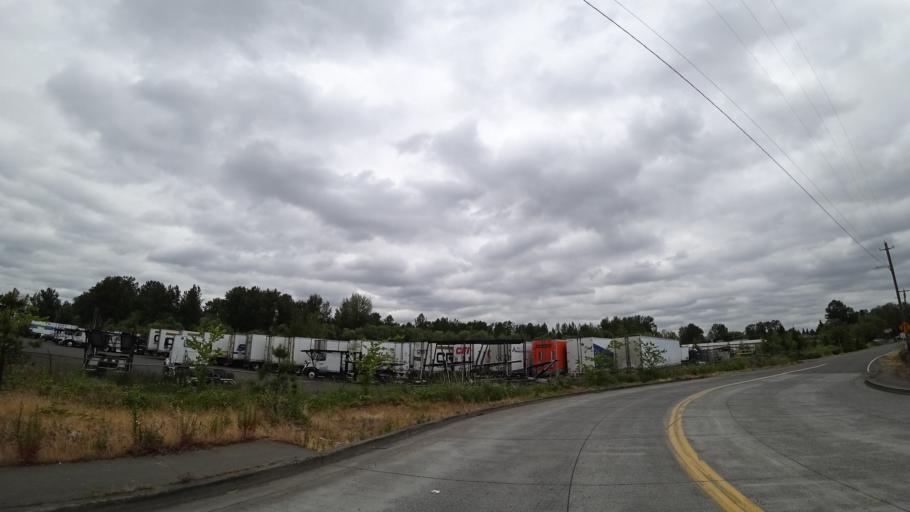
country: US
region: Washington
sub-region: Clark County
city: Vancouver
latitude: 45.5904
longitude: -122.6586
